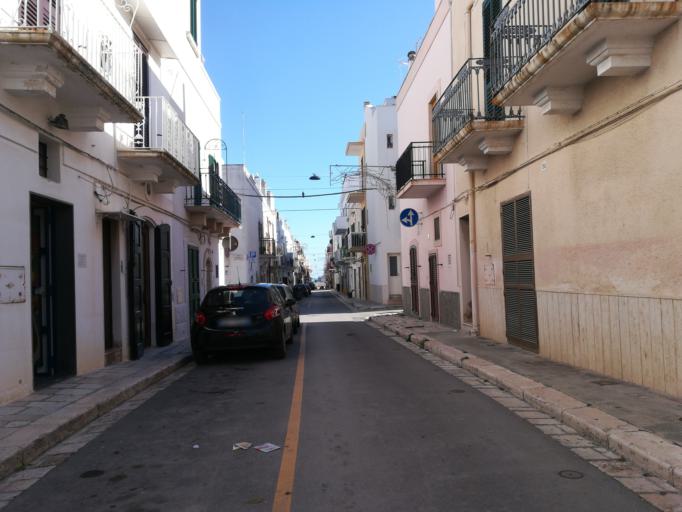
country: IT
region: Apulia
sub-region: Provincia di Bari
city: Polignano a Mare
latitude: 40.9955
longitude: 17.2227
